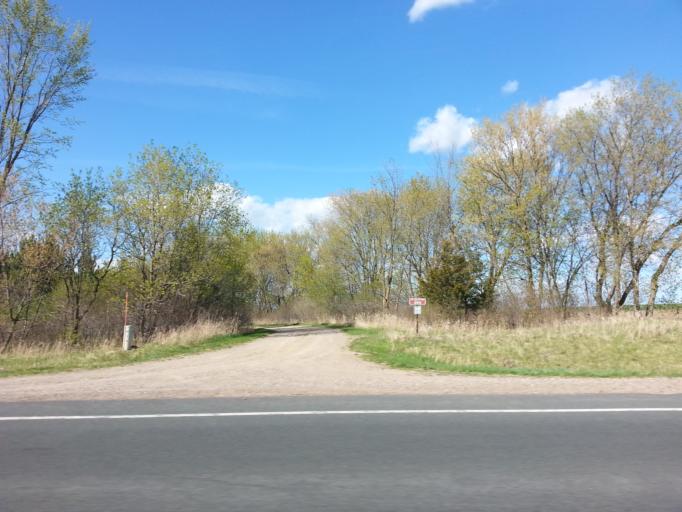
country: US
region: Wisconsin
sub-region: Saint Croix County
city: Somerset
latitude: 45.0441
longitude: -92.6898
